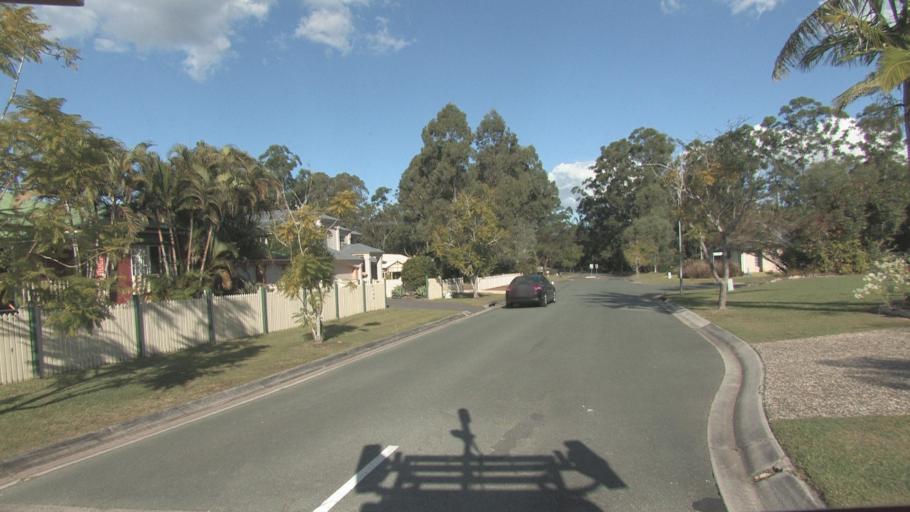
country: AU
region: Queensland
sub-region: Logan
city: Beenleigh
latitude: -27.6618
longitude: 153.2072
